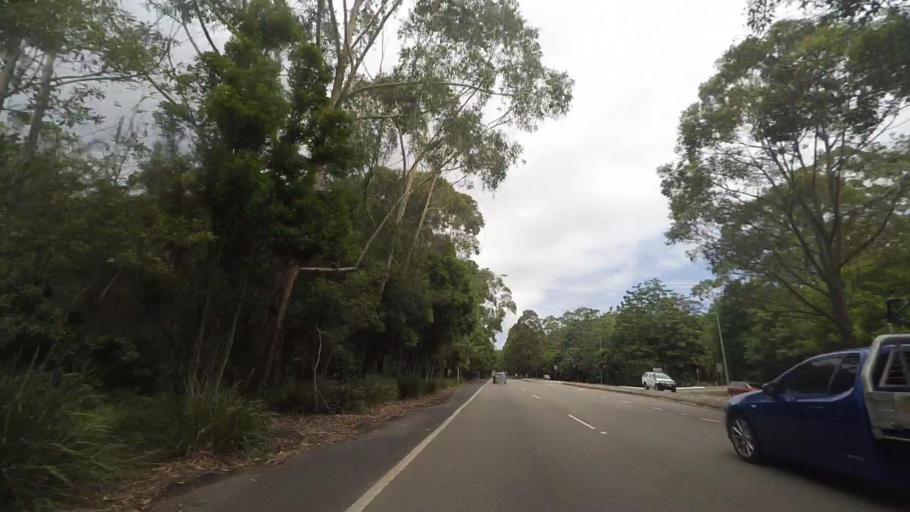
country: AU
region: New South Wales
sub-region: Wyong Shire
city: Berkeley Vale
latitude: -33.3435
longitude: 151.4293
